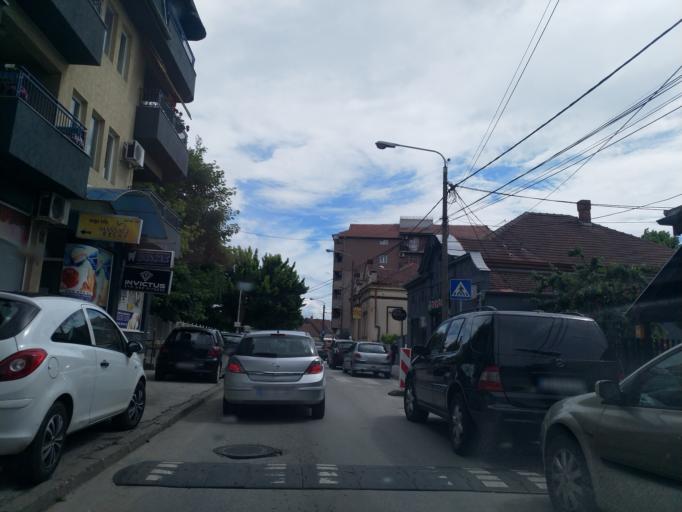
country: RS
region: Central Serbia
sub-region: Pomoravski Okrug
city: Jagodina
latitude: 43.9789
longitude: 21.2577
